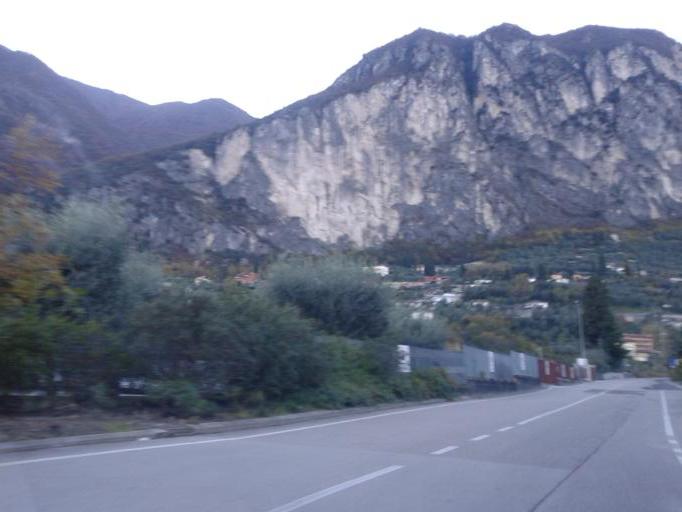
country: IT
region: Trentino-Alto Adige
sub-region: Provincia di Trento
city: Riva del Garda
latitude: 45.8979
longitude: 10.8401
